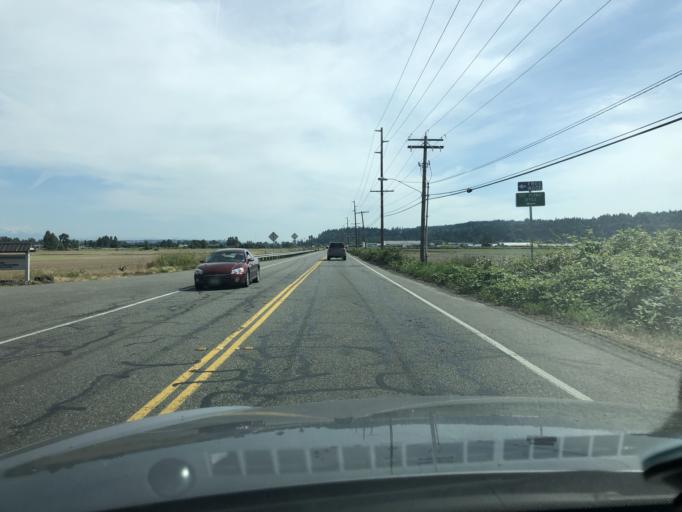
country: US
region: Washington
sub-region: King County
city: Kent
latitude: 47.3631
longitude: -122.2492
